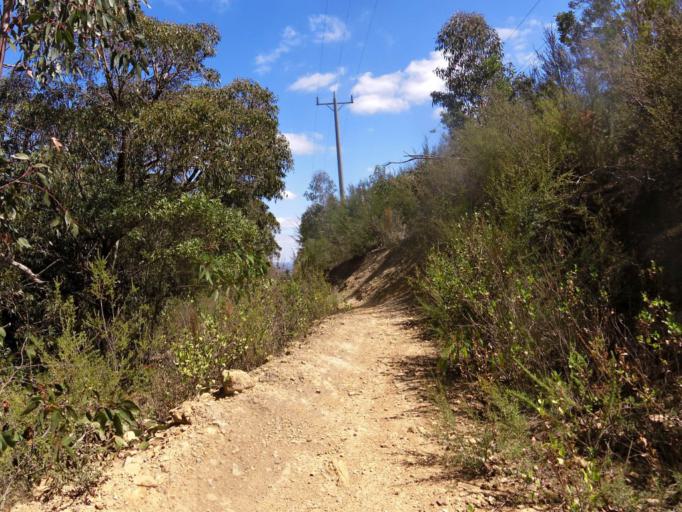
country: AU
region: Victoria
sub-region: Nillumbik
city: Saint Andrews
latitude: -37.5228
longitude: 145.3043
